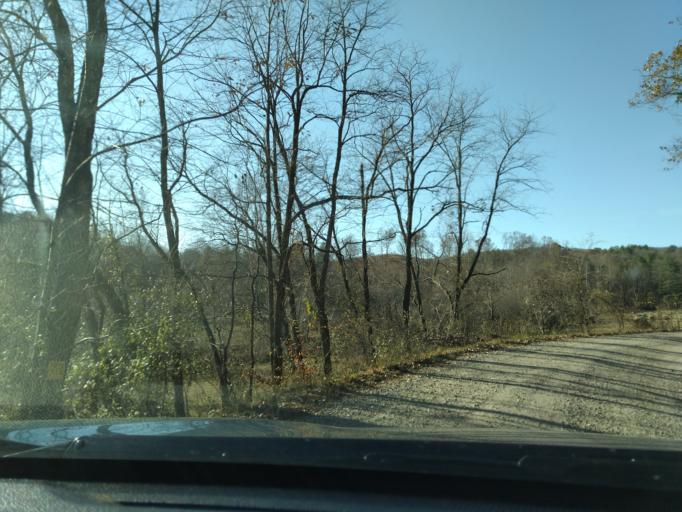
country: US
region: Virginia
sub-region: Floyd County
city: Floyd
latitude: 36.8378
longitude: -80.1884
